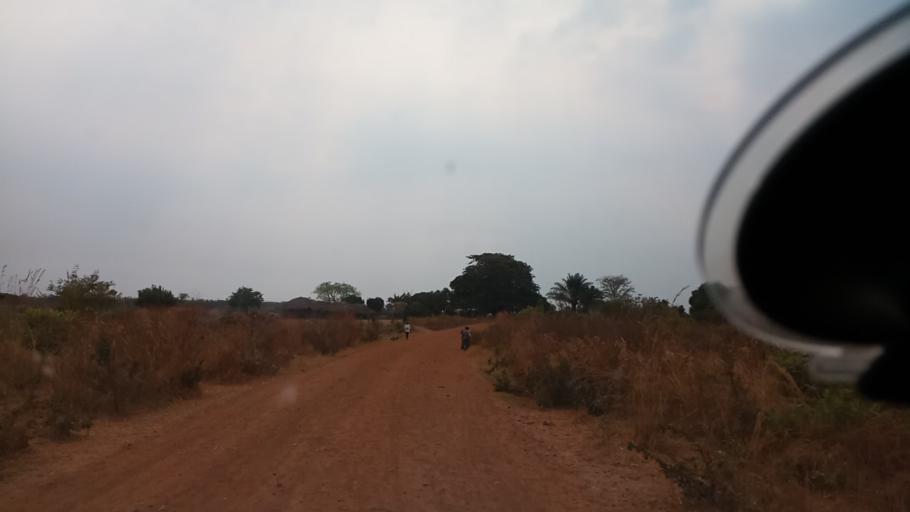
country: ZM
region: Luapula
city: Nchelenge
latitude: -9.0988
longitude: 28.3062
